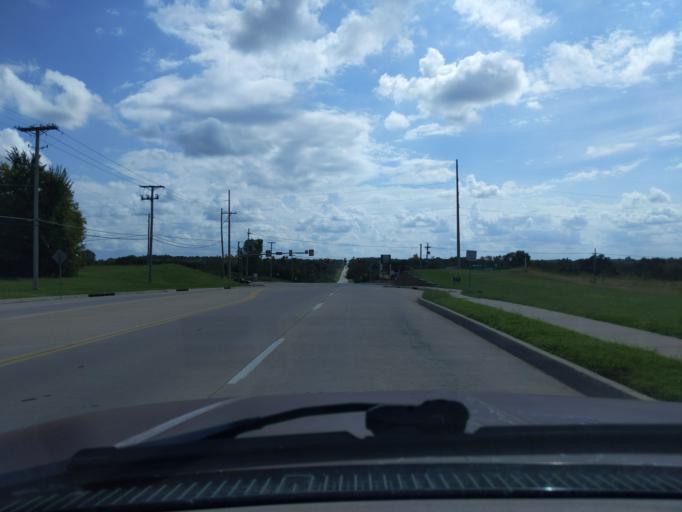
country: US
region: Oklahoma
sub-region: Tulsa County
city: Oakhurst
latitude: 36.0766
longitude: -96.0117
